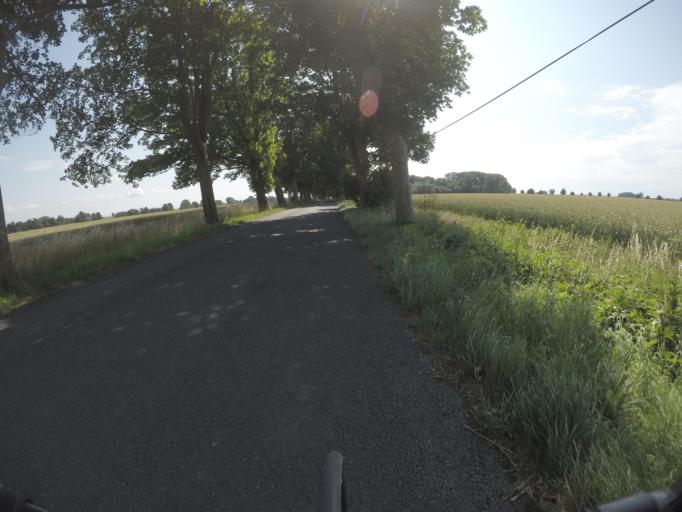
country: DE
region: Mecklenburg-Vorpommern
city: Gingst
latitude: 54.4446
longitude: 13.1892
